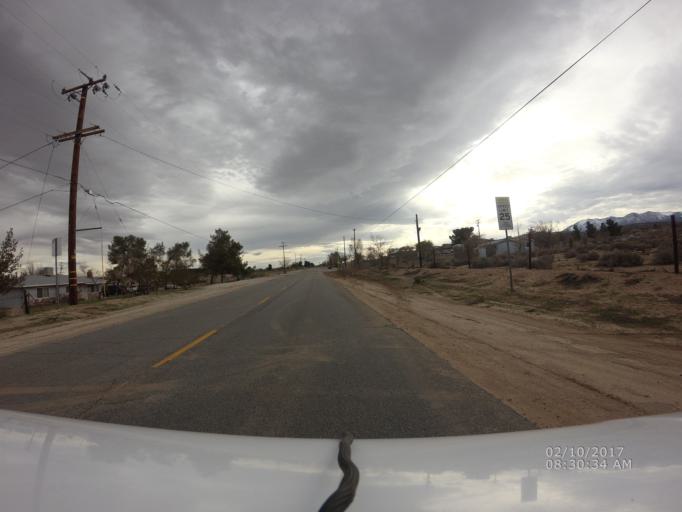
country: US
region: California
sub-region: Los Angeles County
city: Littlerock
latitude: 34.4992
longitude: -117.9020
